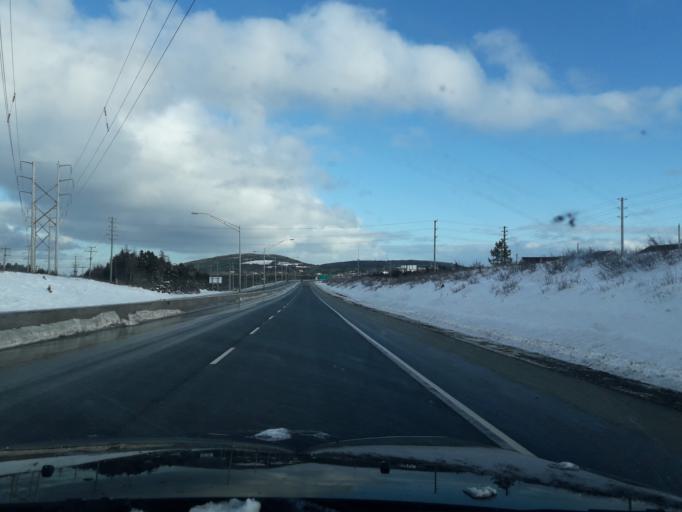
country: CA
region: Newfoundland and Labrador
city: St. John's
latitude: 47.6132
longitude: -52.7048
